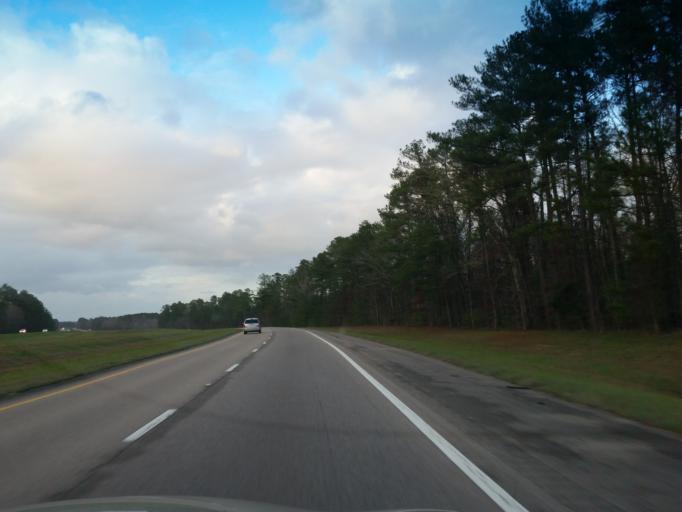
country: US
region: Mississippi
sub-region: Clarke County
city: Stonewall
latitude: 32.0162
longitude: -88.9244
